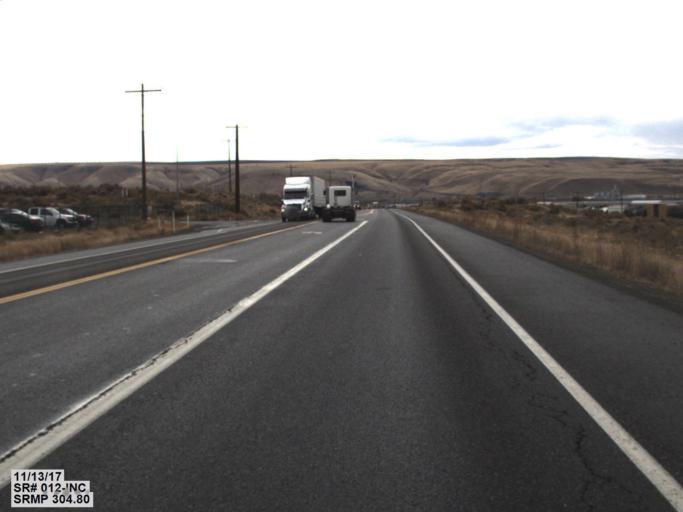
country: US
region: Washington
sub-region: Benton County
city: Finley
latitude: 46.0963
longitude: -118.9119
